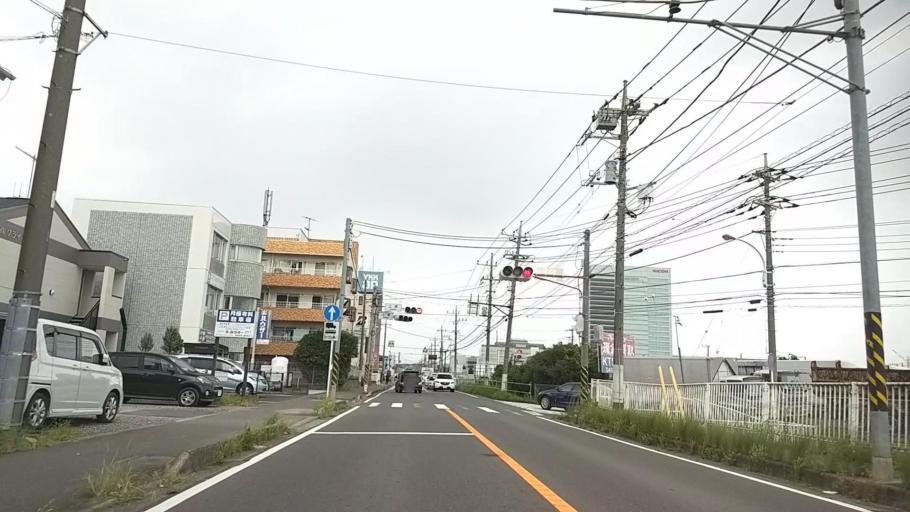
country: JP
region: Kanagawa
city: Atsugi
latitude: 35.4551
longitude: 139.3832
